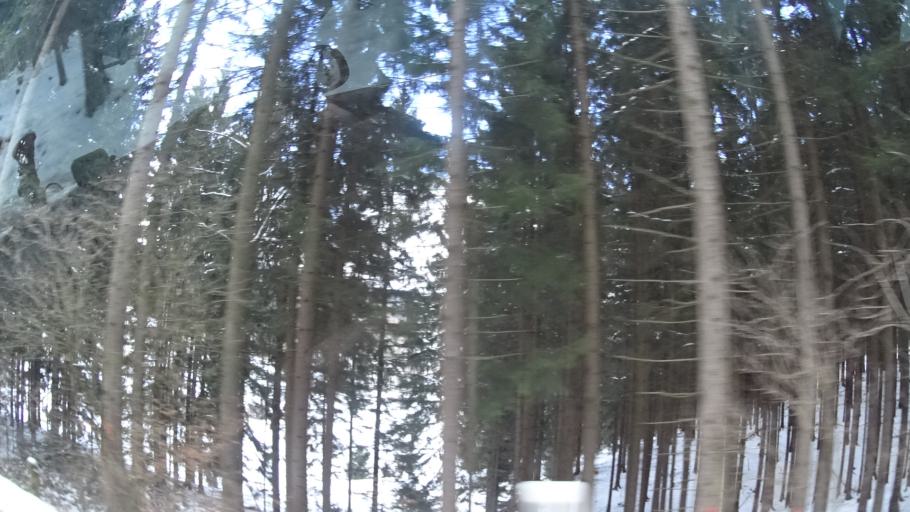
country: DE
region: Thuringia
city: Benshausen
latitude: 50.6324
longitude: 10.6127
